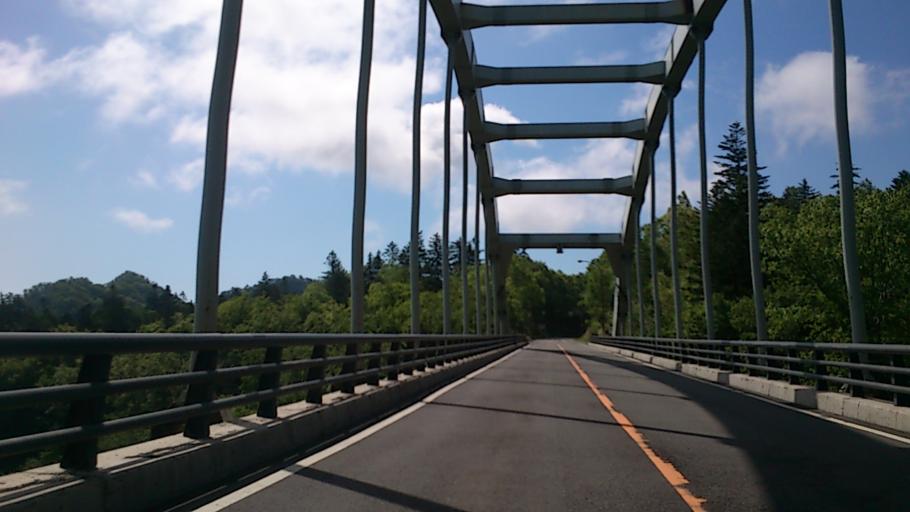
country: JP
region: Hokkaido
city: Shiraoi
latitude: 42.7173
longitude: 141.2070
